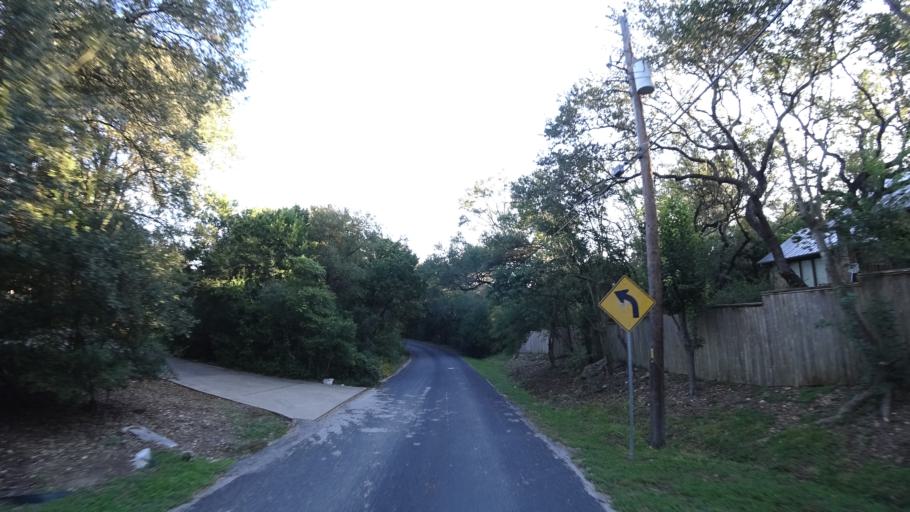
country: US
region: Texas
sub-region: Travis County
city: West Lake Hills
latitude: 30.3466
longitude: -97.8057
